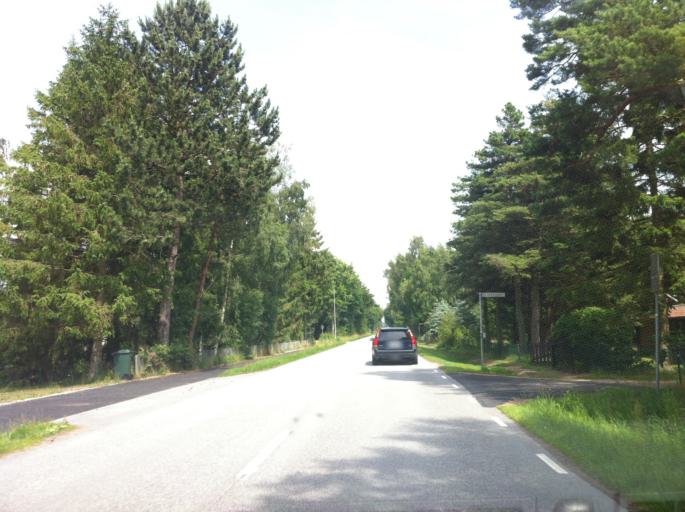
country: SE
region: Skane
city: Smygehamn
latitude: 55.3690
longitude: 13.4430
